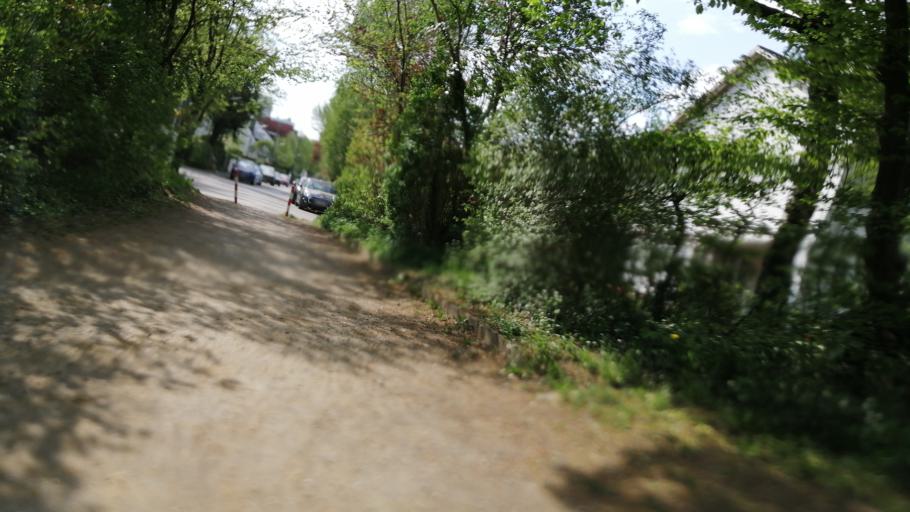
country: DE
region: Bavaria
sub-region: Upper Bavaria
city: Bogenhausen
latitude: 48.1526
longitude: 11.6331
